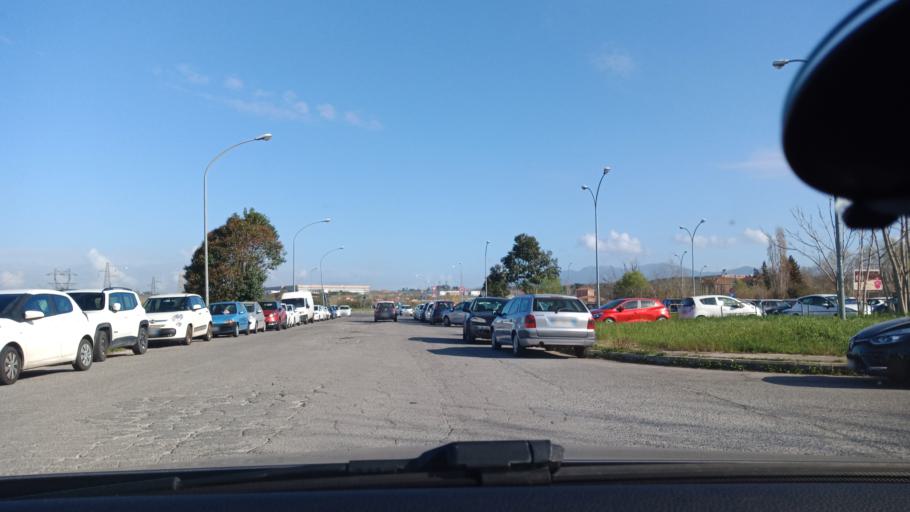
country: IT
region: Latium
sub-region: Citta metropolitana di Roma Capitale
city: Fiano Romano
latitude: 42.1555
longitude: 12.6453
